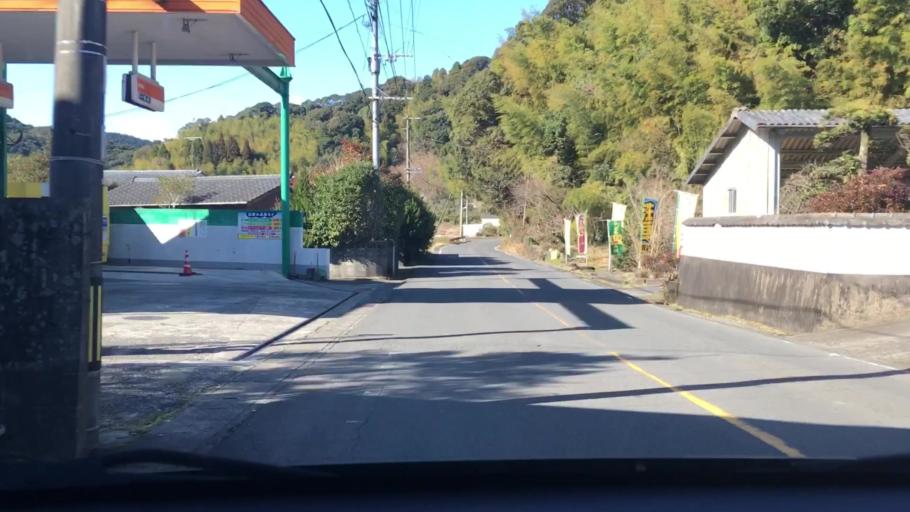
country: JP
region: Kagoshima
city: Satsumasendai
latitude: 31.7793
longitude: 130.3998
